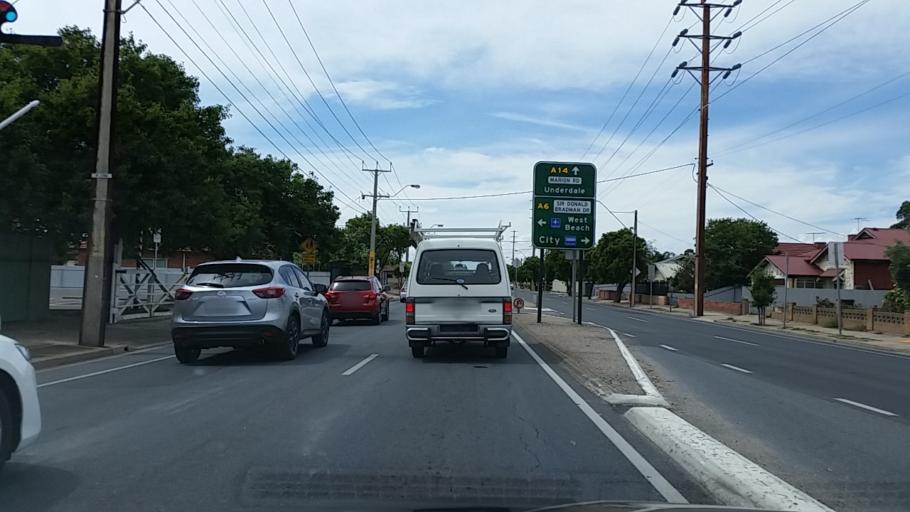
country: AU
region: South Australia
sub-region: City of West Torrens
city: Plympton
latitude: -34.9353
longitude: 138.5527
